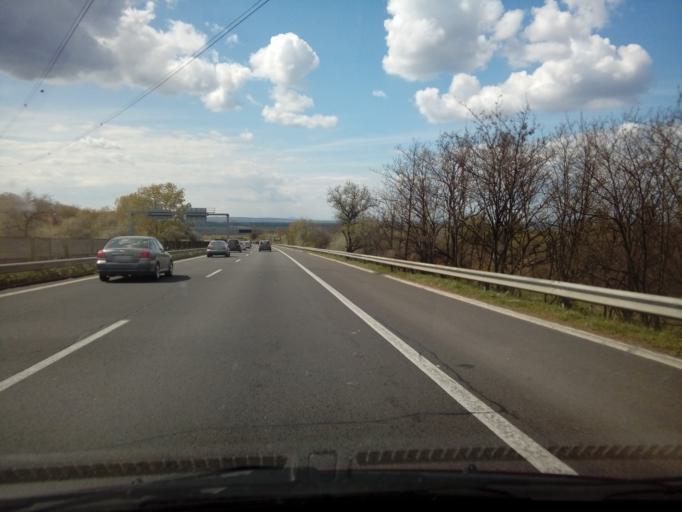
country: HU
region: Heves
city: Hatvan
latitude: 47.6865
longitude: 19.7036
